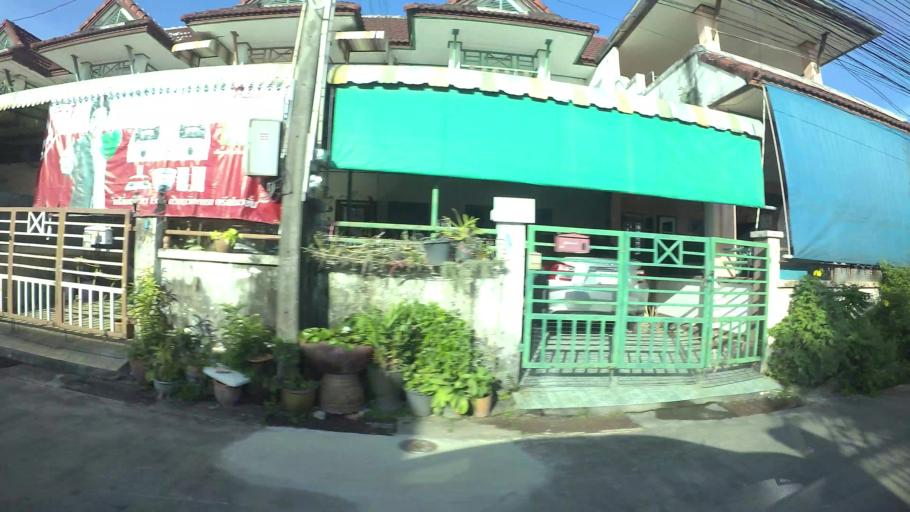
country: TH
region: Rayong
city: Rayong
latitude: 12.6916
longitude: 101.2777
